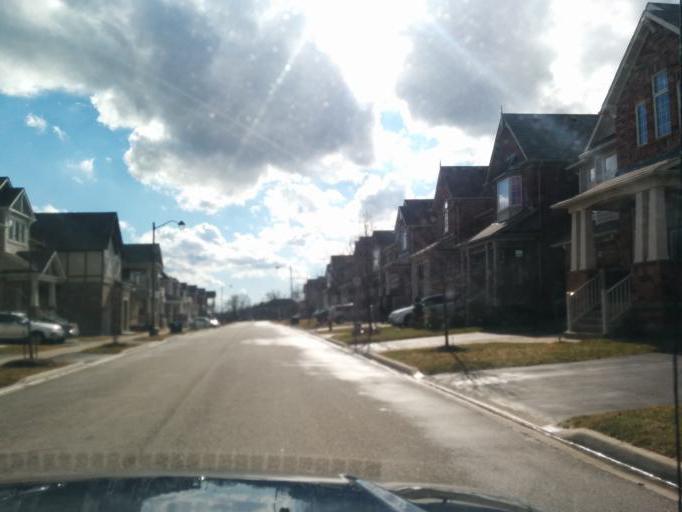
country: CA
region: Ontario
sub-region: Halton
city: Milton
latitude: 43.5045
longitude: -79.8512
